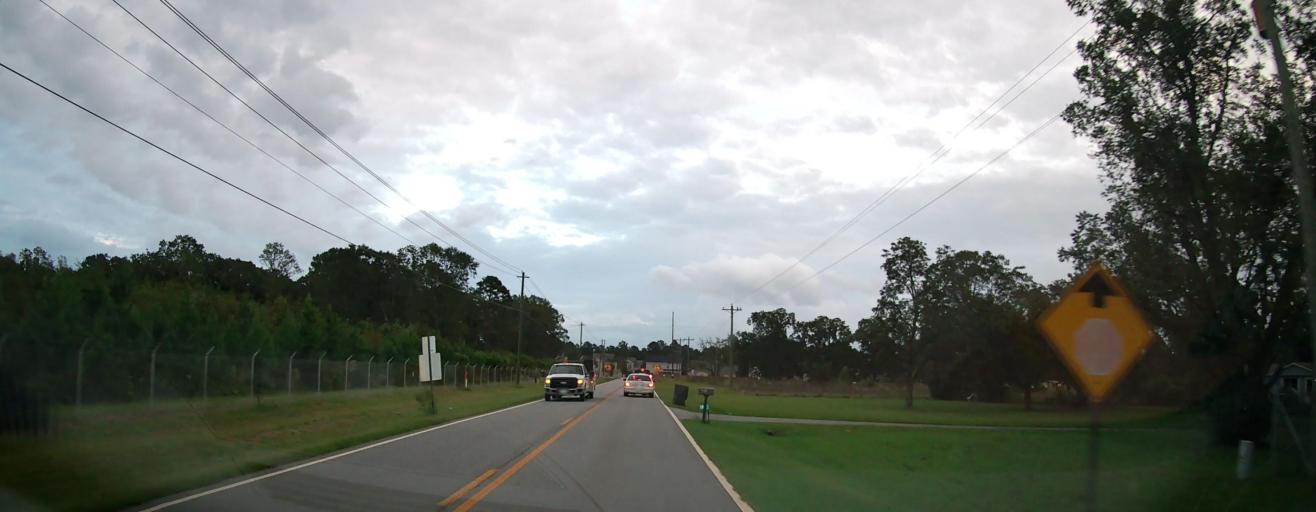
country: US
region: Georgia
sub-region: Houston County
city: Centerville
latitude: 32.6513
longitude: -83.7112
